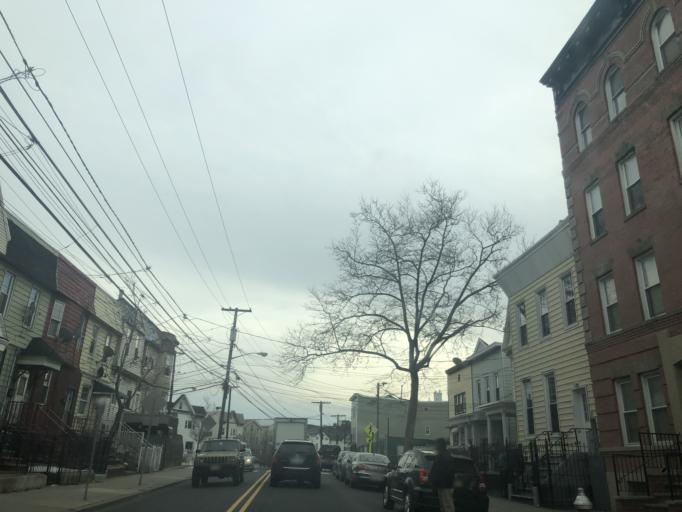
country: US
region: New Jersey
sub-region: Hudson County
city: Jersey City
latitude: 40.7226
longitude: -74.0658
